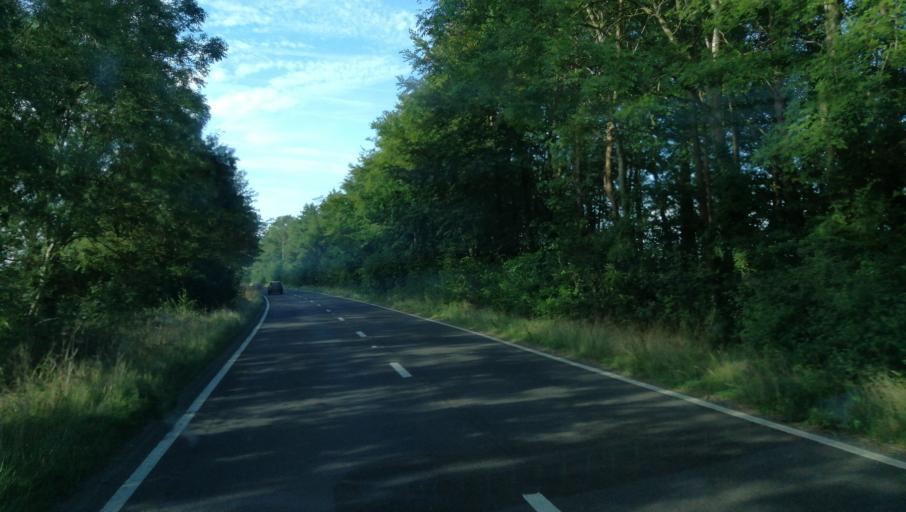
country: GB
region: England
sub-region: Oxfordshire
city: Deddington
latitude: 51.9426
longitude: -1.3249
